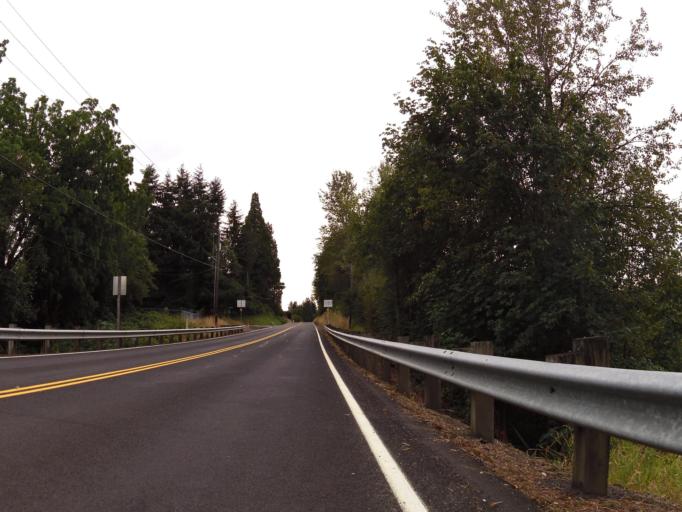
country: US
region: Washington
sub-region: Cowlitz County
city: Castle Rock
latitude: 46.2347
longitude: -122.8897
